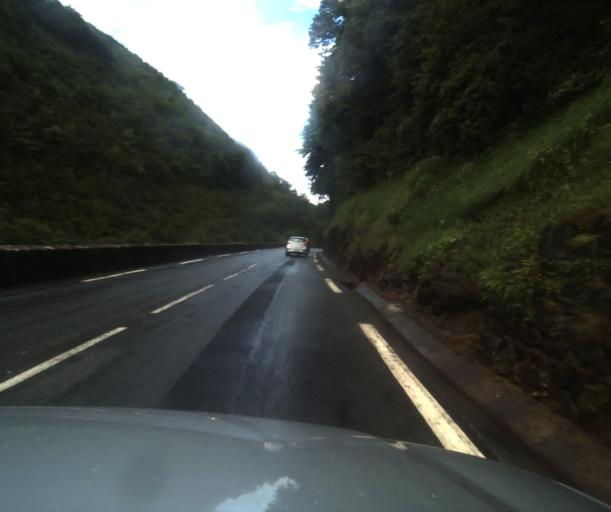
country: FR
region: Midi-Pyrenees
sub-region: Departement des Hautes-Pyrenees
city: Pierrefitte-Nestalas
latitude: 42.9249
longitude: -0.0417
